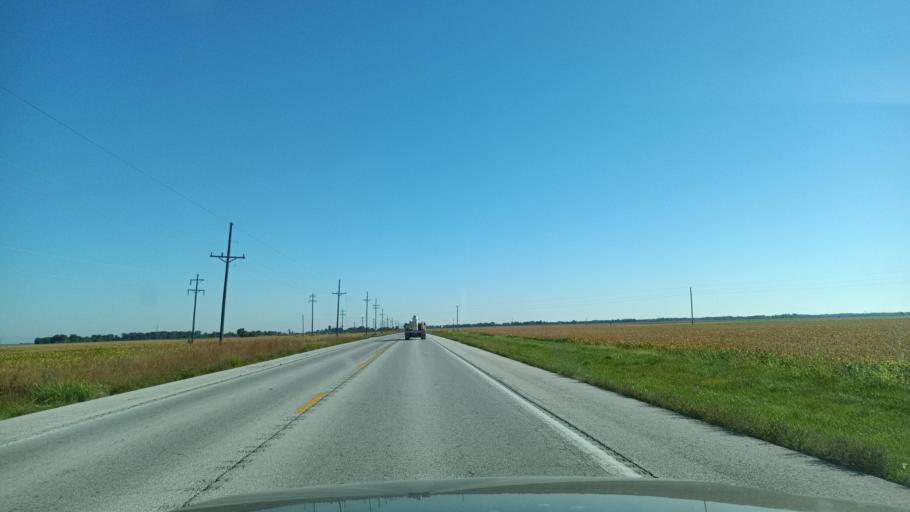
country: US
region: Missouri
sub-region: Audrain County
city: Vandalia
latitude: 39.4755
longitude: -91.5879
